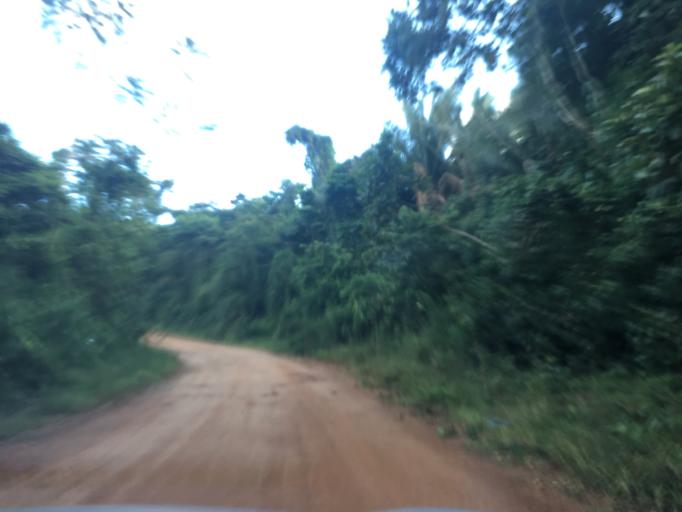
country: BZ
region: Stann Creek
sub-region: Dangriga
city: Dangriga
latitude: 16.7976
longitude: -88.3978
